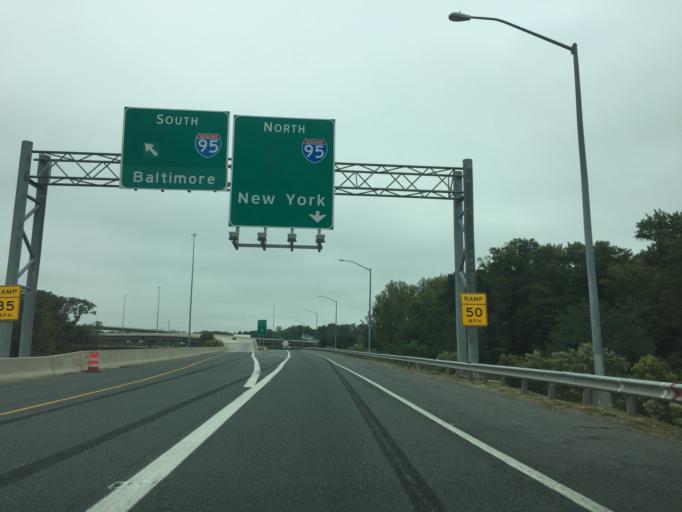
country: US
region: Maryland
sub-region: Baltimore County
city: Rossville
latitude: 39.3465
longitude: -76.4935
